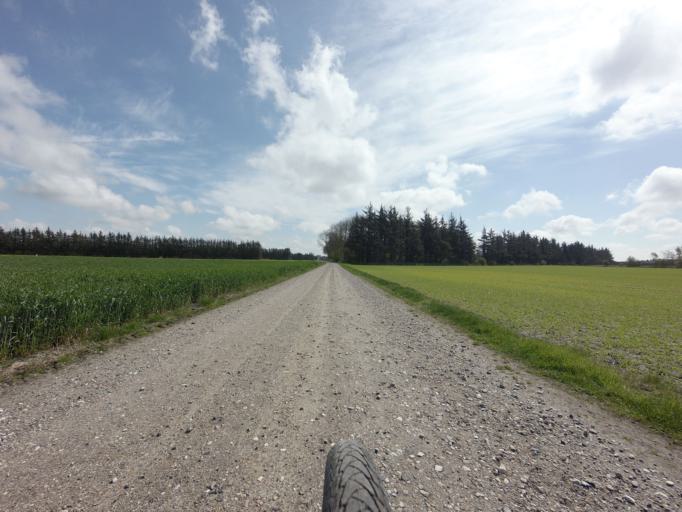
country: DK
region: North Denmark
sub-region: Jammerbugt Kommune
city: Kas
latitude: 57.2002
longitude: 9.6060
